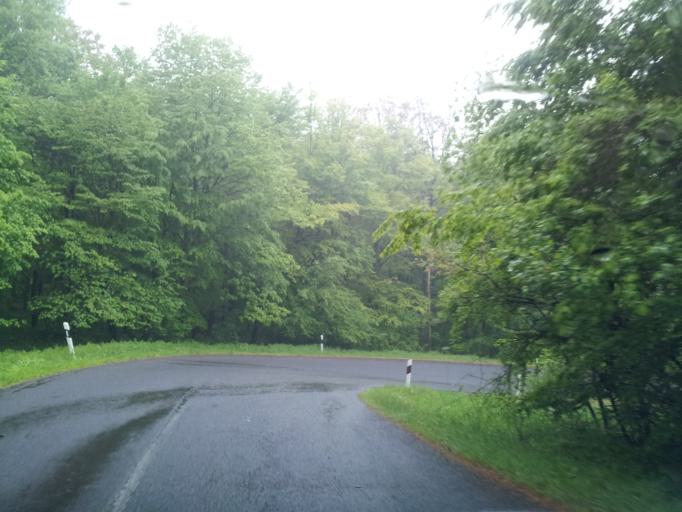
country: HU
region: Baranya
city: Hosszuheteny
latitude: 46.1870
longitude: 18.3201
